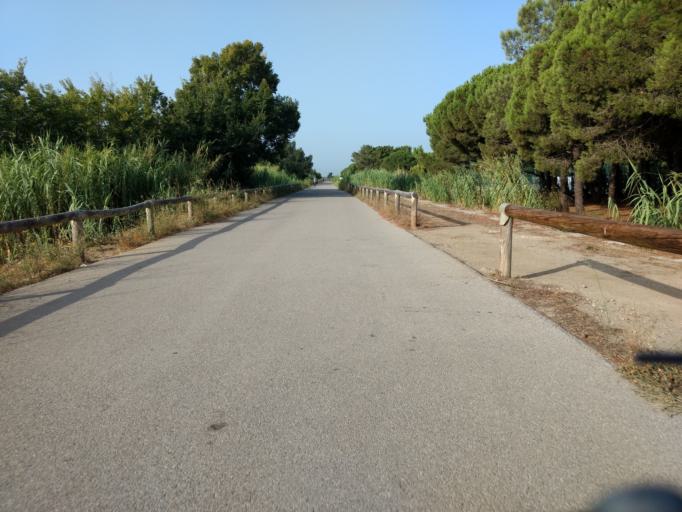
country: FR
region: Languedoc-Roussillon
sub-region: Departement des Pyrenees-Orientales
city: Le Barcares
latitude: 42.7766
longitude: 3.0301
